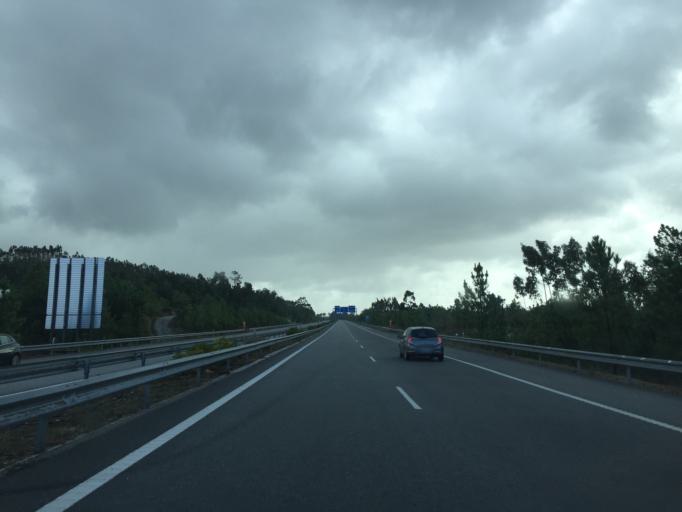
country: PT
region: Aveiro
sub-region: Mealhada
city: Pampilhosa do Botao
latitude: 40.2810
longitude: -8.5107
